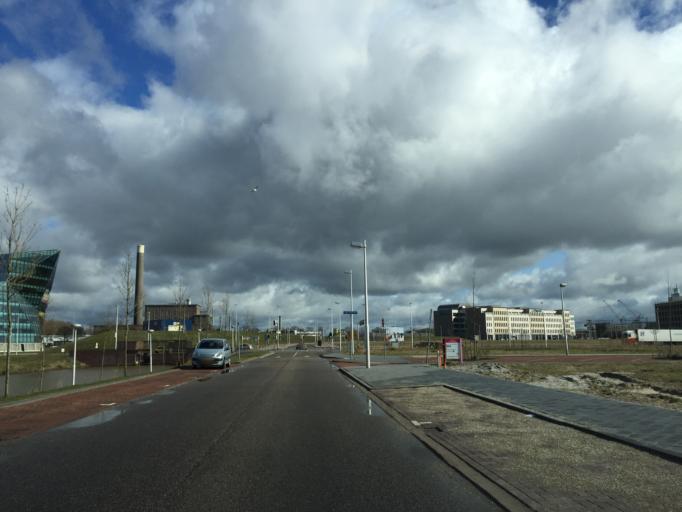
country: NL
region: Utrecht
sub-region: Stichtse Vecht
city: Maarssen
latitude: 52.1016
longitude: 5.0589
